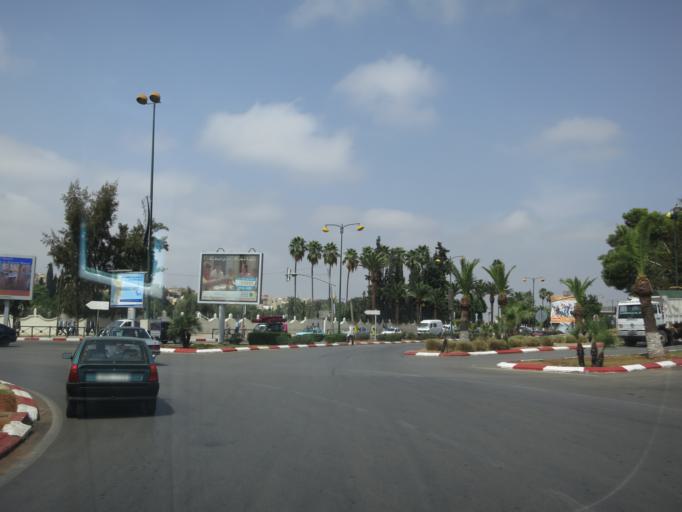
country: MA
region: Meknes-Tafilalet
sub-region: Meknes
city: Meknes
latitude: 33.8961
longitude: -5.5558
